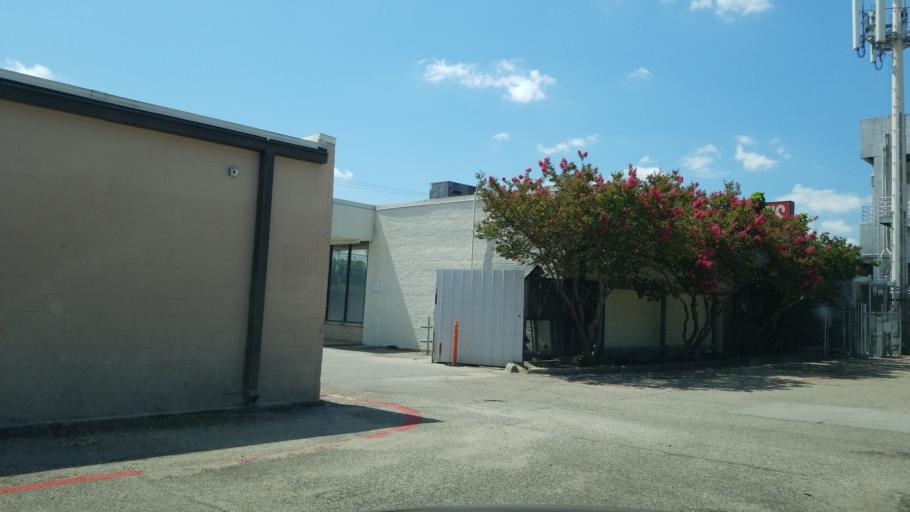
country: US
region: Texas
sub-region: Dallas County
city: Farmers Branch
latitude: 32.8792
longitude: -96.8555
